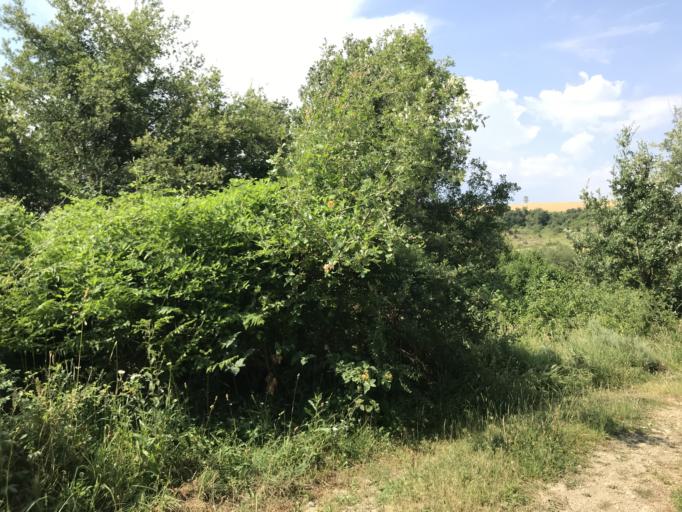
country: ES
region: Basque Country
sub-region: Provincia de Alava
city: Gasteiz / Vitoria
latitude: 42.8156
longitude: -2.6447
